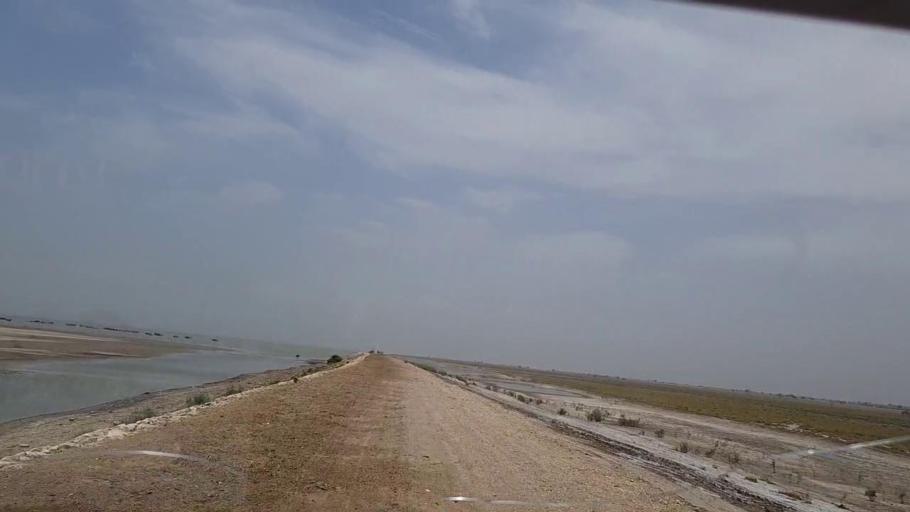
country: PK
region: Sindh
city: Sehwan
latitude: 26.4168
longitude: 67.7494
